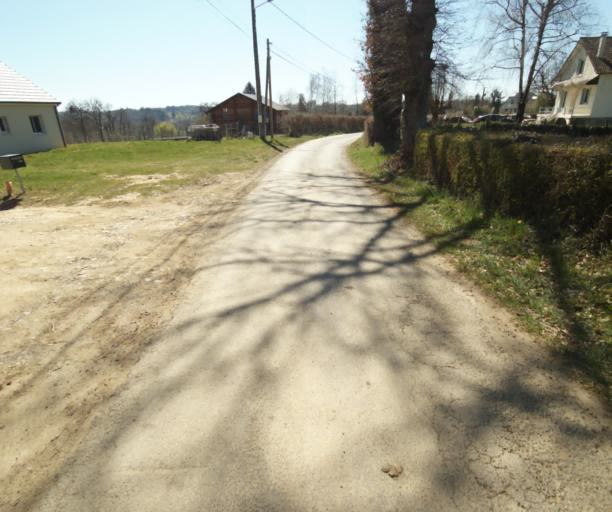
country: FR
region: Limousin
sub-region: Departement de la Correze
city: Chamboulive
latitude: 45.4373
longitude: 1.6898
